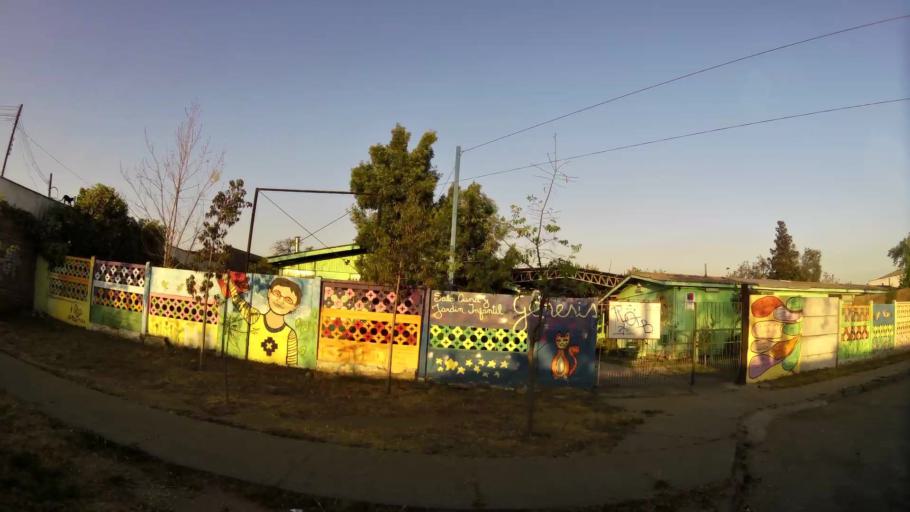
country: CL
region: Santiago Metropolitan
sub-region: Provincia de Santiago
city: Santiago
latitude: -33.5092
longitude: -70.6285
